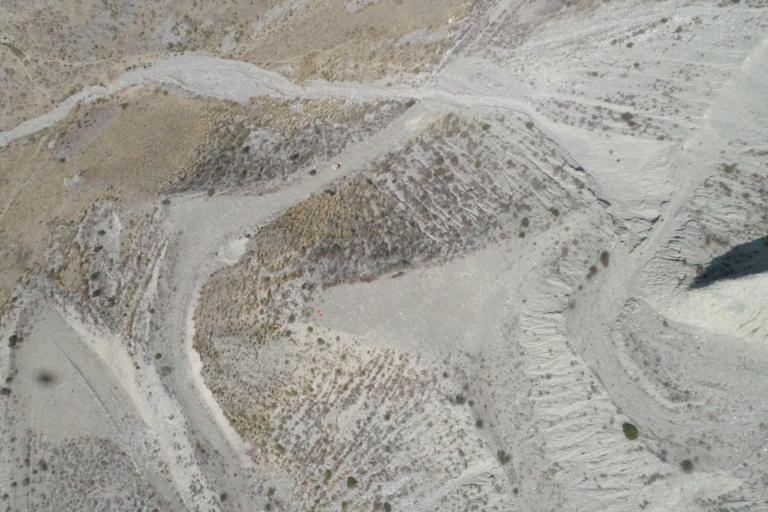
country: BO
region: La Paz
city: La Paz
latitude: -16.4721
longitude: -68.0969
